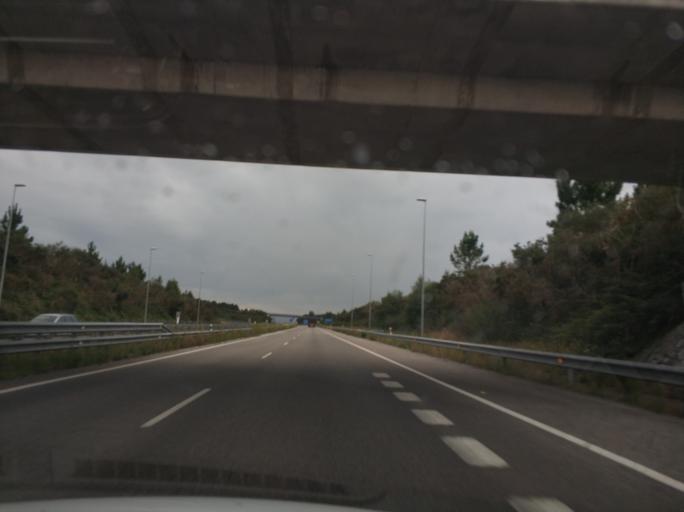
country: ES
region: Asturias
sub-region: Province of Asturias
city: Tapia de Casariego
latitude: 43.5465
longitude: -6.9209
